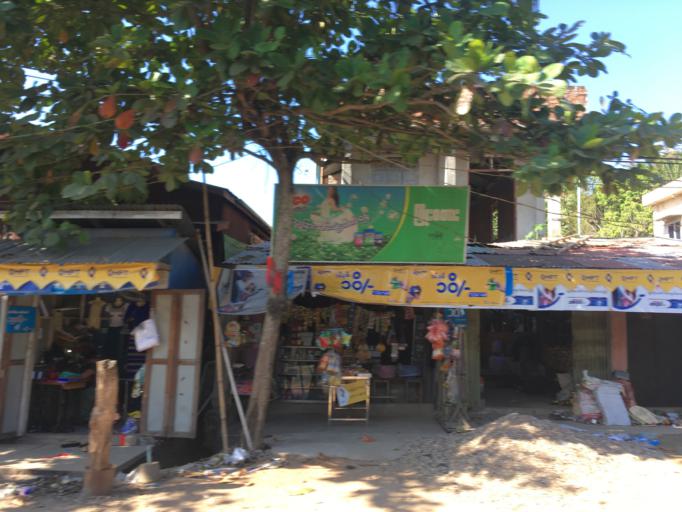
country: MM
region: Mon
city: Mawlamyine
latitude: 16.4851
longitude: 97.6316
